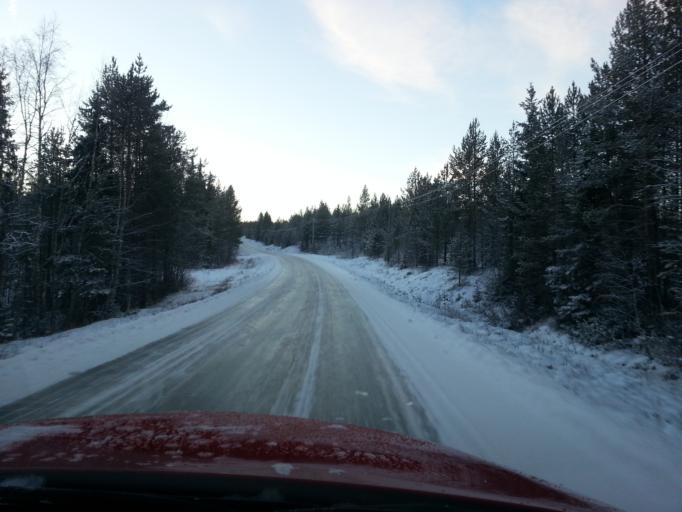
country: SE
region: Jaemtland
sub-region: Harjedalens Kommun
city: Sveg
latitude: 62.3943
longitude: 13.5106
